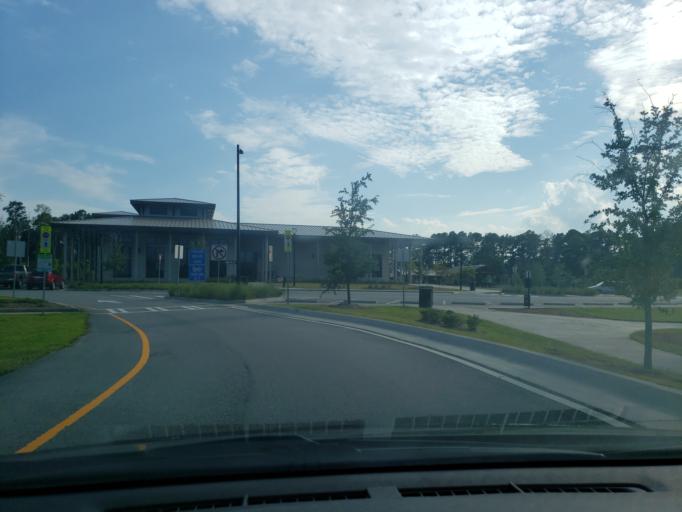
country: US
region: Georgia
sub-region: Chatham County
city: Port Wentworth
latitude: 32.2176
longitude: -81.1741
